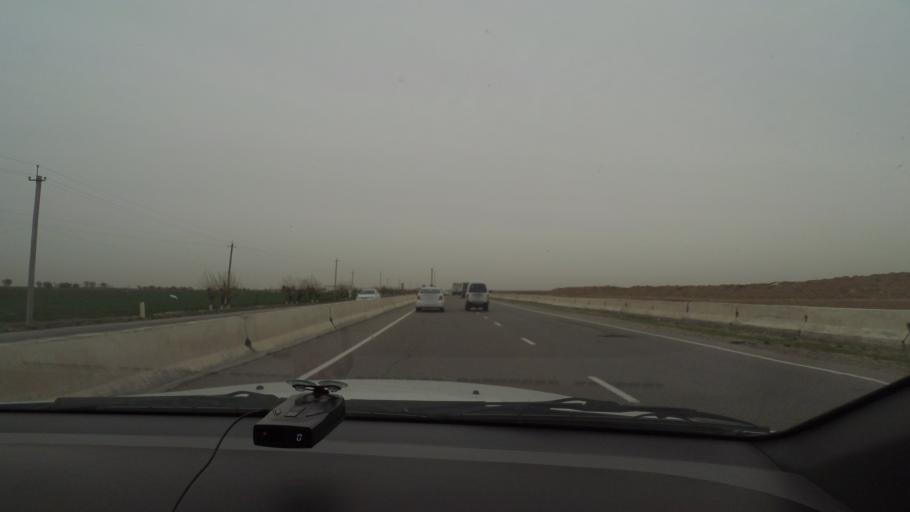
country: UZ
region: Jizzax
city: Gagarin
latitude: 40.4532
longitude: 68.2523
